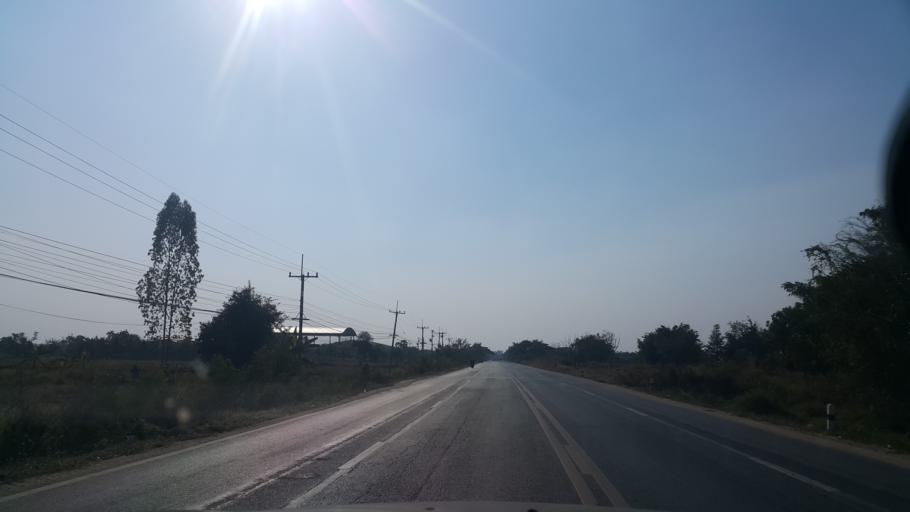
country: TH
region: Nakhon Ratchasima
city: Phimai
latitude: 15.2126
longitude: 102.4733
